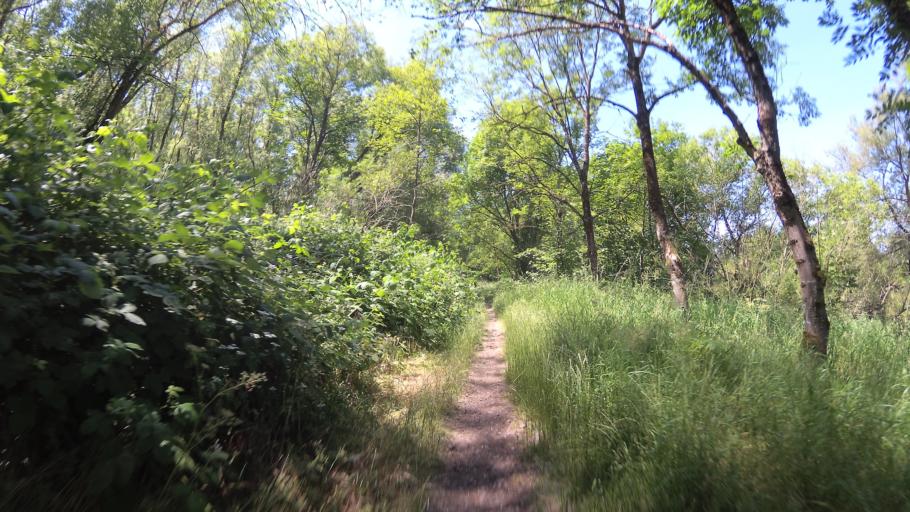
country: DE
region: Saarland
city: Nalbach
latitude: 49.3670
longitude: 6.7691
